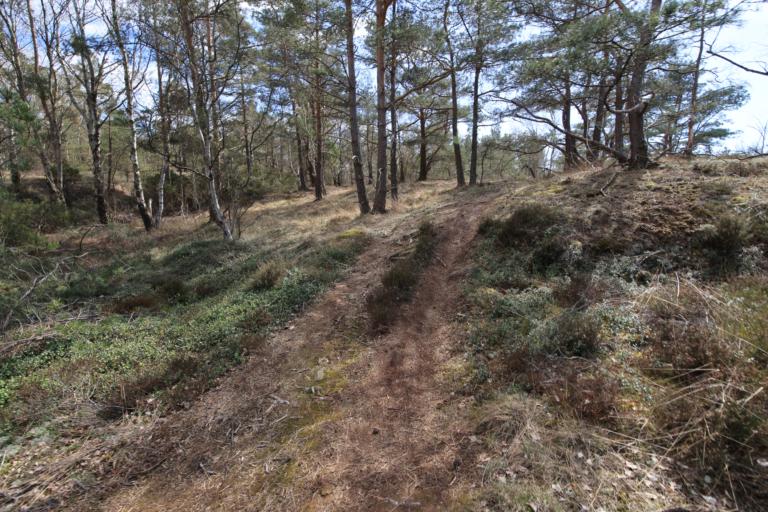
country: SE
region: Halland
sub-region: Varbergs Kommun
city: Varberg
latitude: 57.1767
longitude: 12.2351
